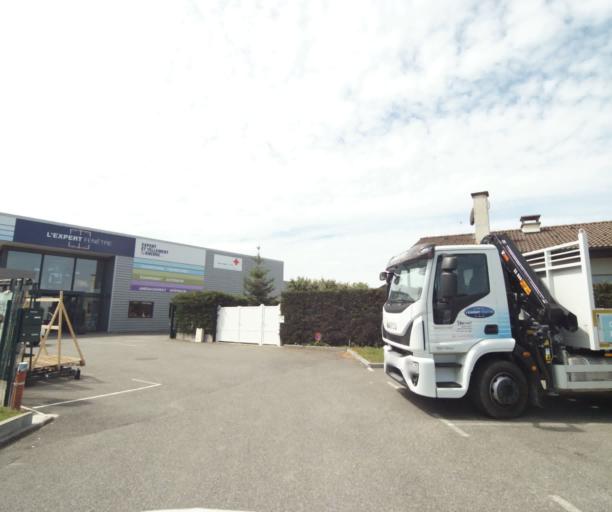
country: FR
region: Rhone-Alpes
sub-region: Departement de la Haute-Savoie
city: Anthy-sur-Leman
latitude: 46.3496
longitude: 6.4353
